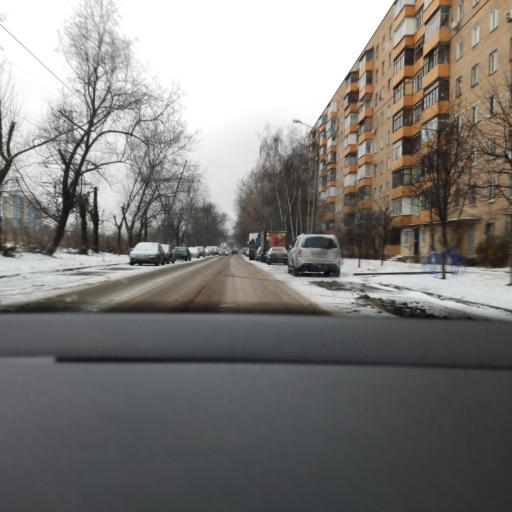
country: RU
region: Moskovskaya
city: Reutov
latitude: 55.7686
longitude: 37.8533
